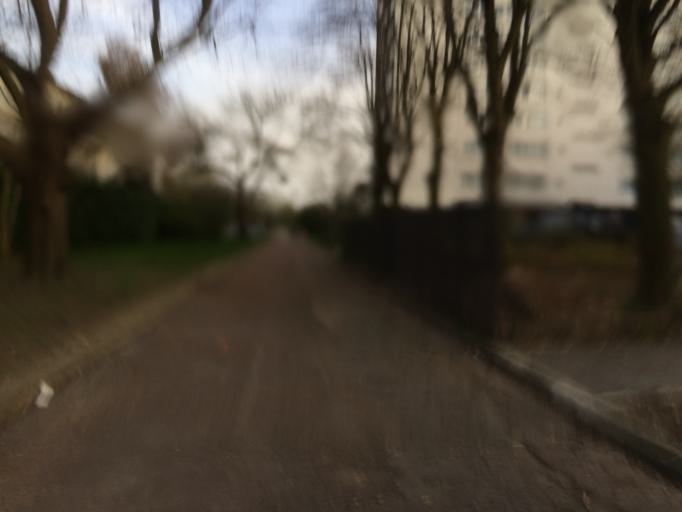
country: FR
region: Ile-de-France
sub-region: Departement de l'Essonne
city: Massy
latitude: 48.7338
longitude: 2.2943
